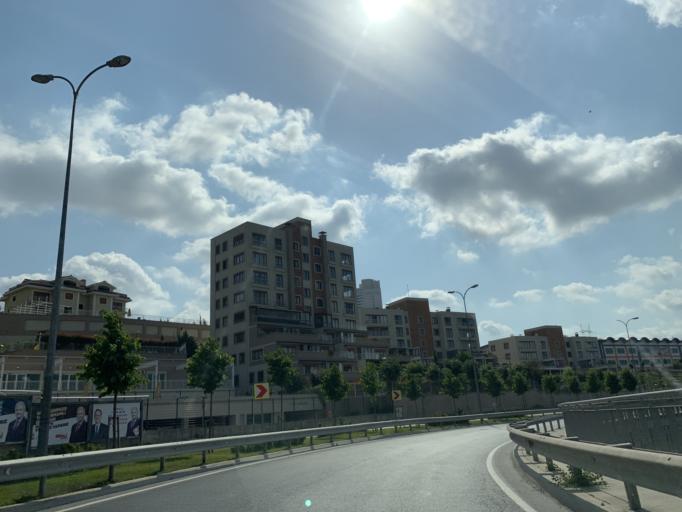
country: TR
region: Istanbul
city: Esenyurt
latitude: 41.0794
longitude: 28.6828
